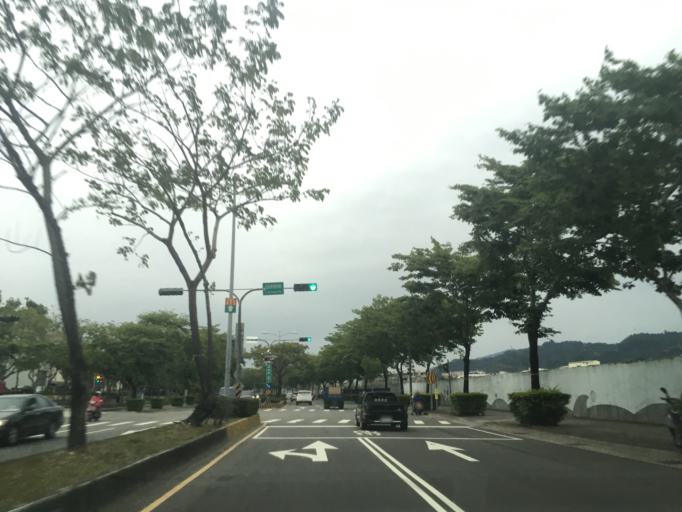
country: TW
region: Taiwan
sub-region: Taichung City
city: Taichung
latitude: 24.1376
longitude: 120.7189
